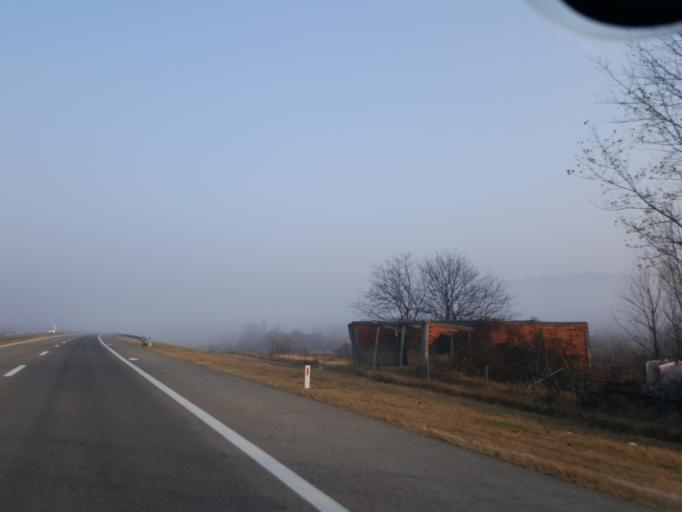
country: RS
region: Central Serbia
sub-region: Jablanicki Okrug
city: Leskovac
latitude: 42.9977
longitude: 22.0253
